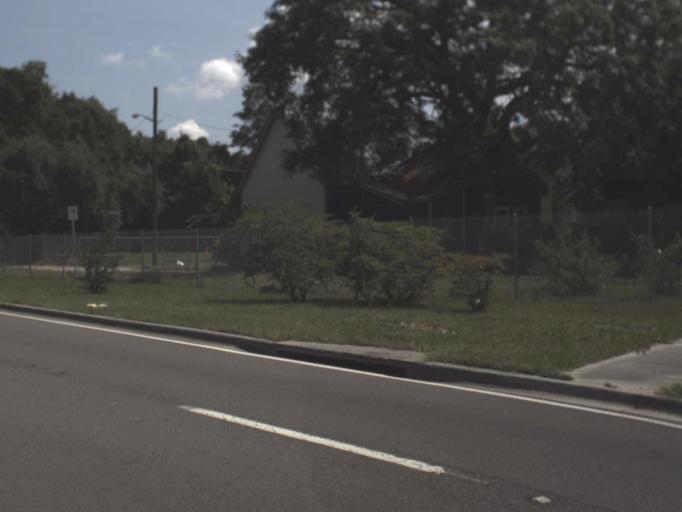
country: US
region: Florida
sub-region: Duval County
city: Jacksonville
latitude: 30.3286
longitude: -81.6365
